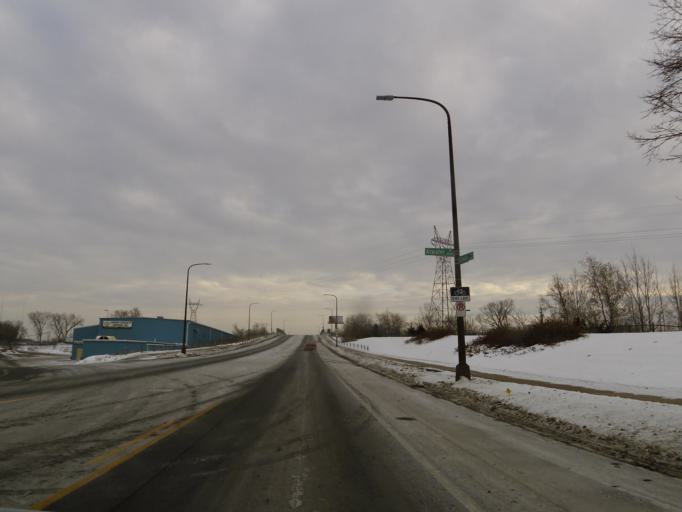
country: US
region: Minnesota
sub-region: Ramsey County
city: Saint Paul
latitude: 44.9666
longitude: -93.1200
